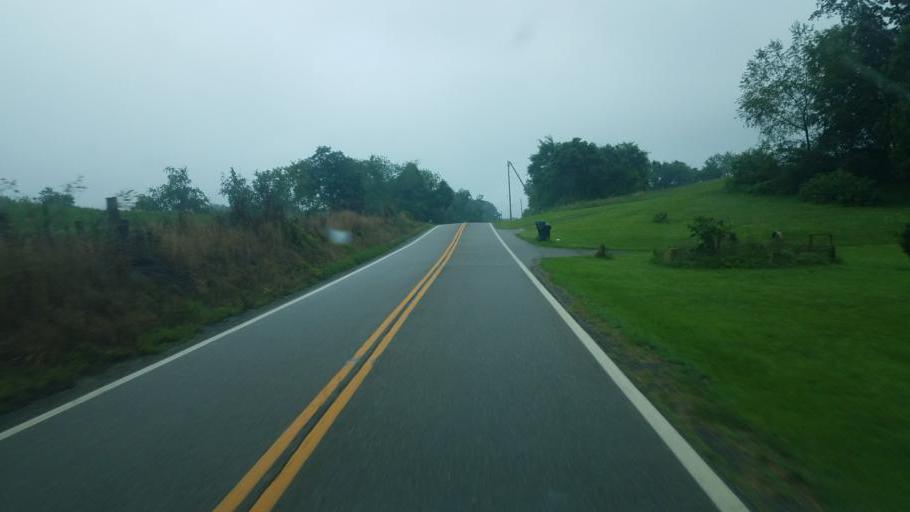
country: US
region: Ohio
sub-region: Tuscarawas County
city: Rockford
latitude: 40.4502
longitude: -81.1660
